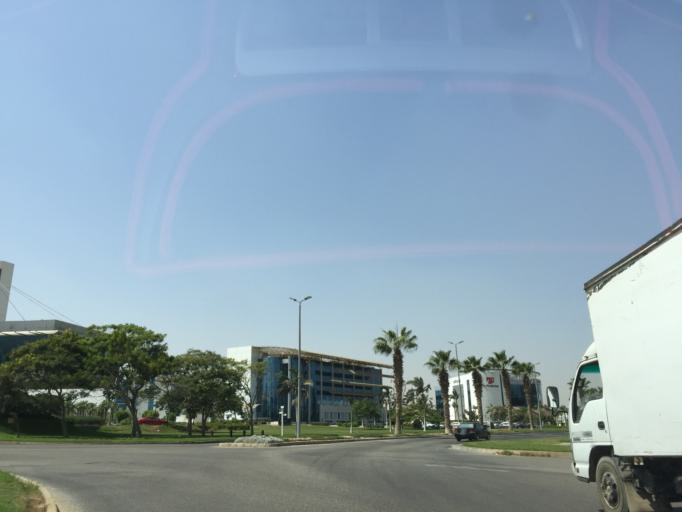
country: EG
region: Al Jizah
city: Awsim
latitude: 30.0699
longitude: 31.0181
